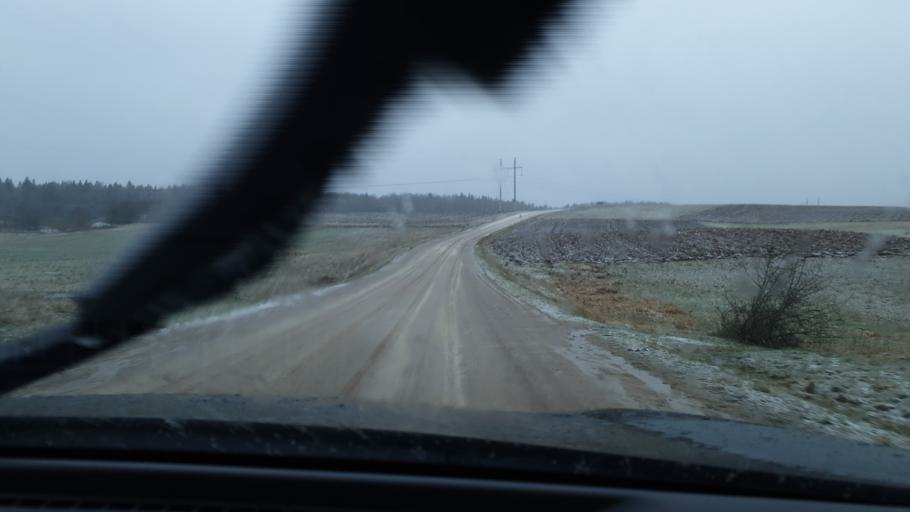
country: LT
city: Jieznas
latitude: 54.5535
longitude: 24.3147
